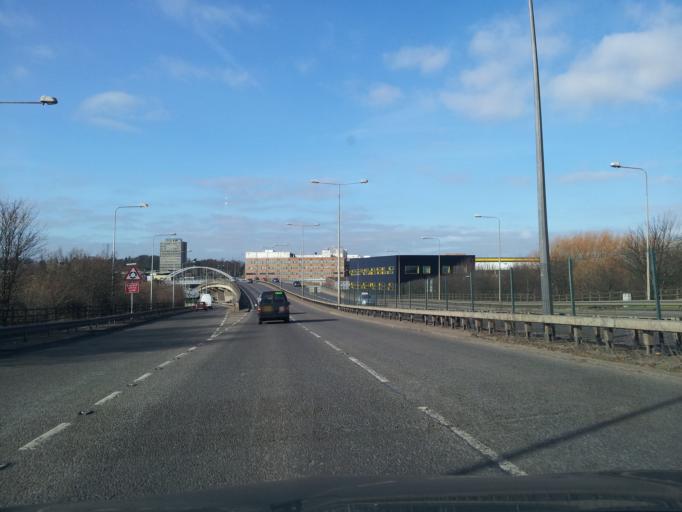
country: GB
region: England
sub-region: Nottingham
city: Nottingham
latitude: 52.9394
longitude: -1.1789
